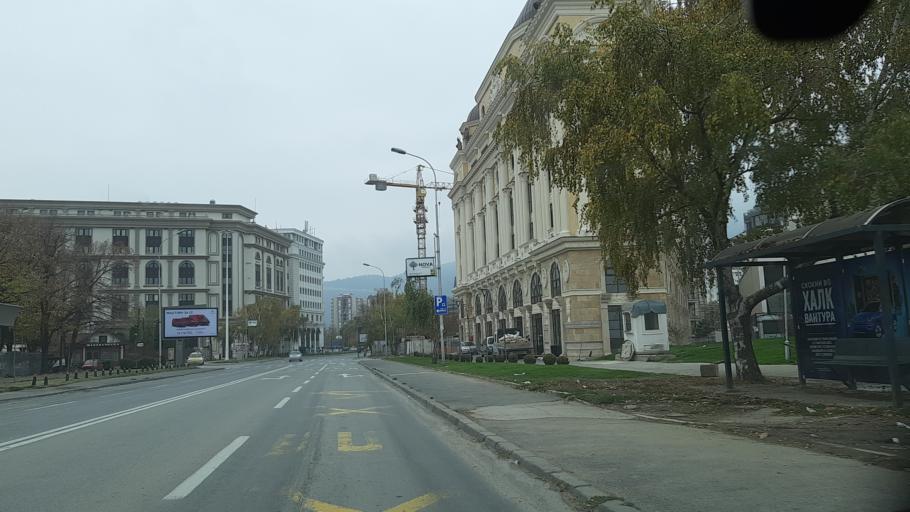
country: MK
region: Karpos
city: Skopje
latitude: 41.9978
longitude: 21.4381
